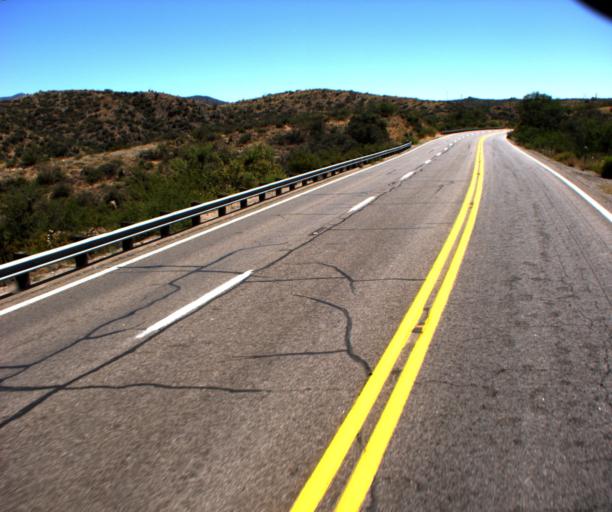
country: US
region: Arizona
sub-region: Pinal County
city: Oracle
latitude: 32.6351
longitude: -110.7341
